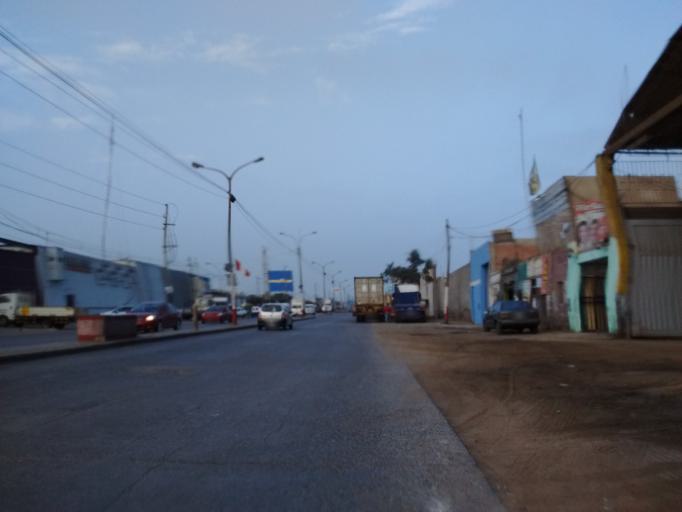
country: PE
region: Callao
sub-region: Callao
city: Callao
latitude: -12.0474
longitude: -77.0862
